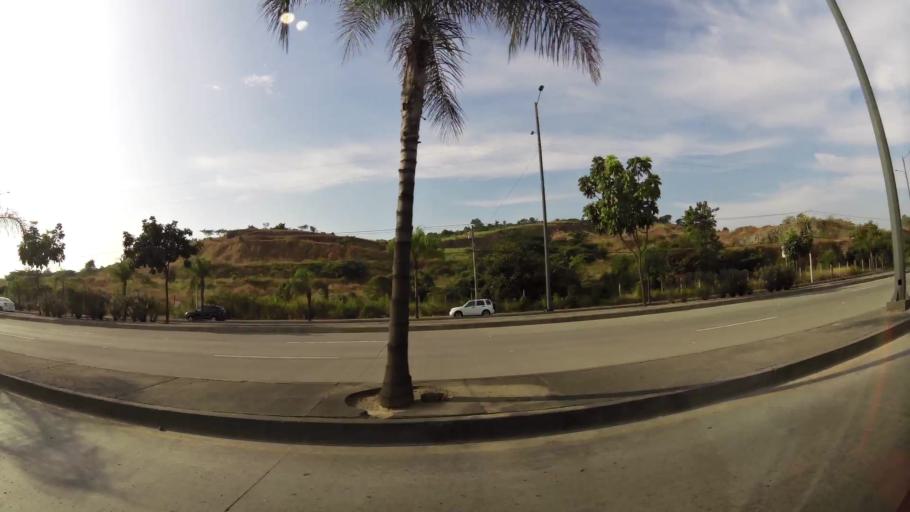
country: EC
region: Guayas
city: Eloy Alfaro
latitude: -2.0705
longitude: -79.9155
